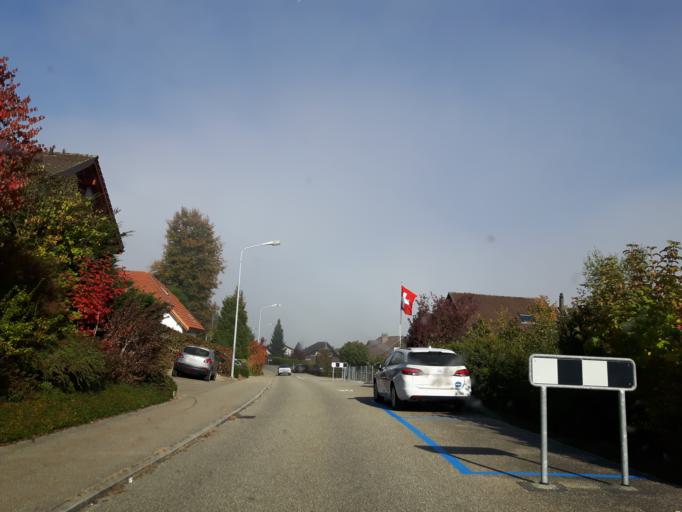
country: CH
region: Bern
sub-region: Oberaargau
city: Roggwil
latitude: 47.2332
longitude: 7.8298
